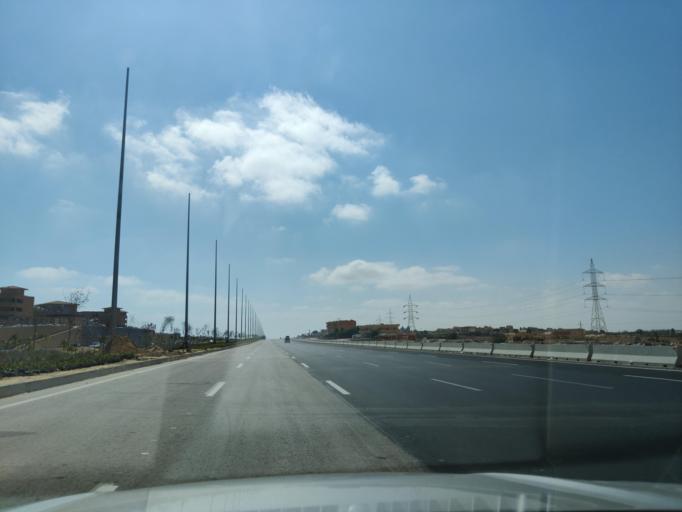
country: EG
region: Muhafazat Matruh
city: Al `Alamayn
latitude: 30.9931
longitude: 28.6678
